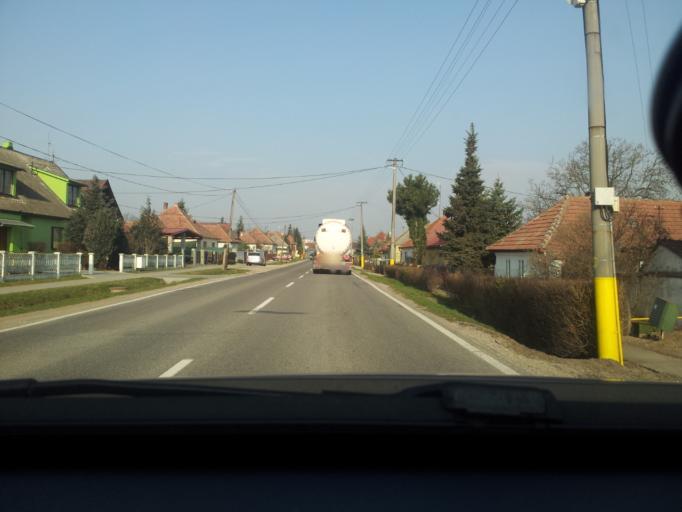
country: SK
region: Trnavsky
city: Hlohovec
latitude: 48.3644
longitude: 17.9069
